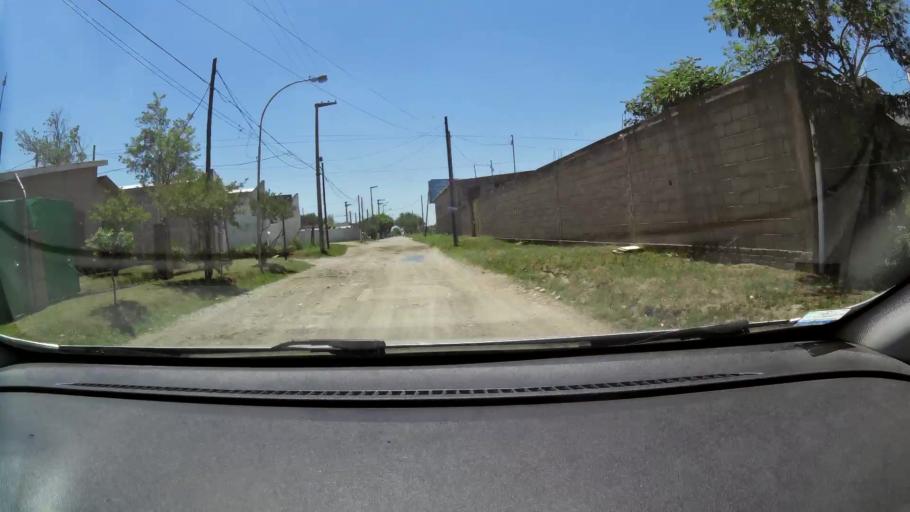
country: AR
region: Cordoba
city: Malvinas Argentinas
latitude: -31.3803
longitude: -64.1280
